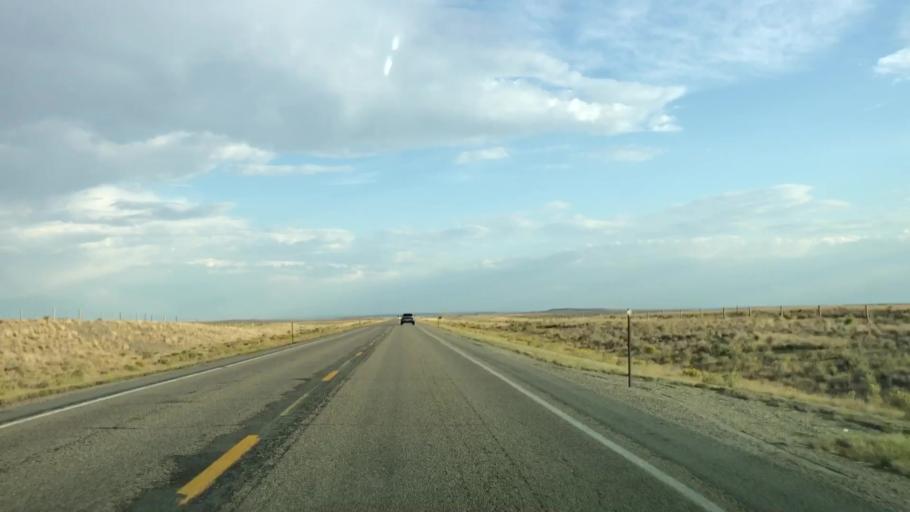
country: US
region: Wyoming
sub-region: Sublette County
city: Pinedale
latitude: 42.4059
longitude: -109.5495
